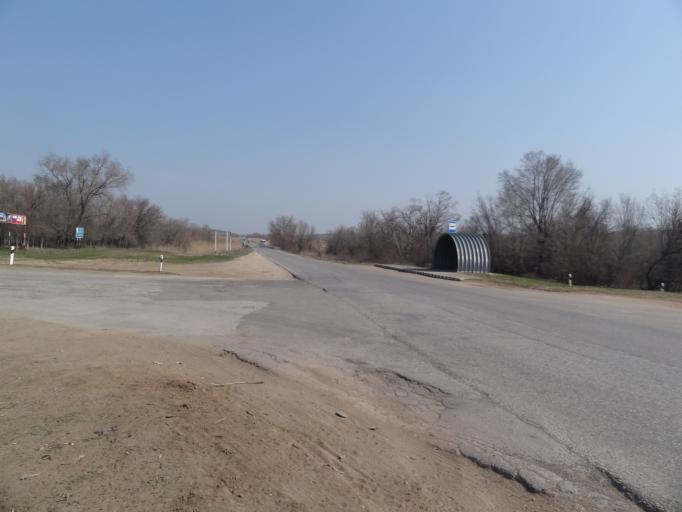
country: RU
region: Saratov
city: Privolzhskiy
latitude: 51.2491
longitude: 45.9375
